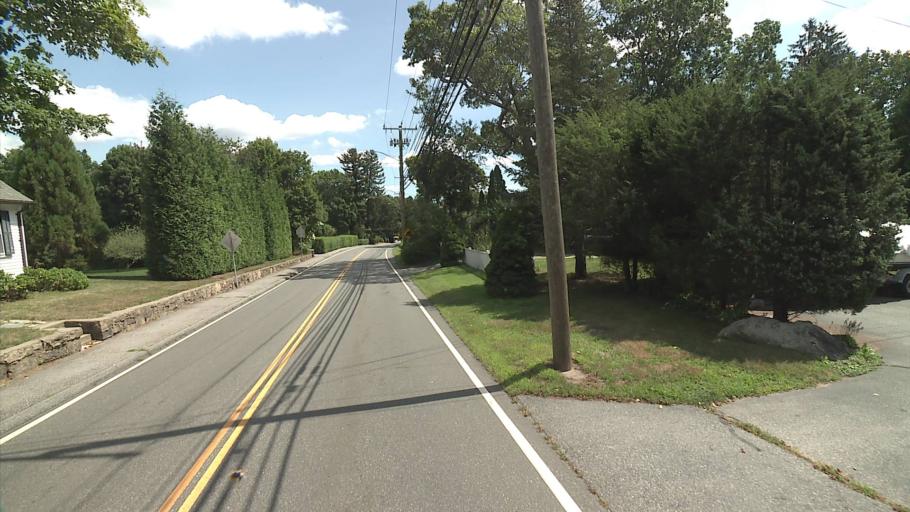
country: US
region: Connecticut
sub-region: New London County
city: Mystic
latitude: 41.3530
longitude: -71.9799
